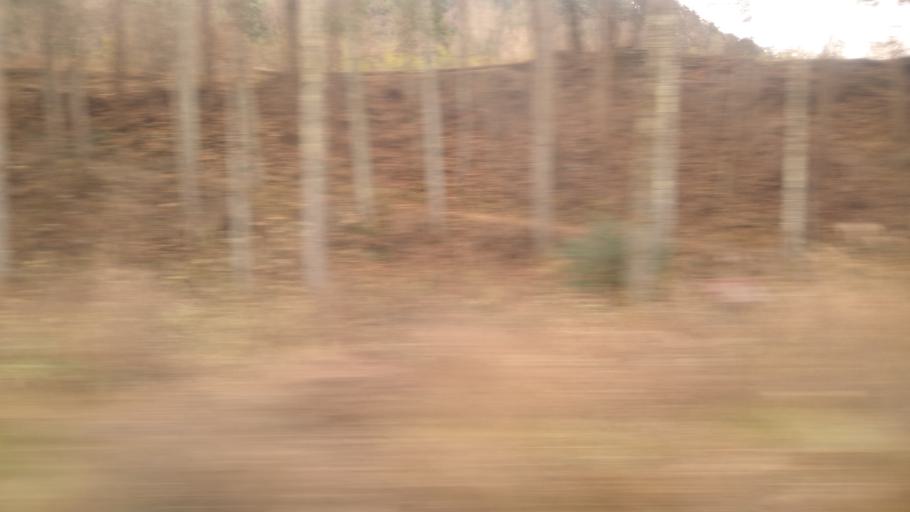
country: JP
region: Nagano
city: Ina
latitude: 35.8858
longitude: 137.7617
